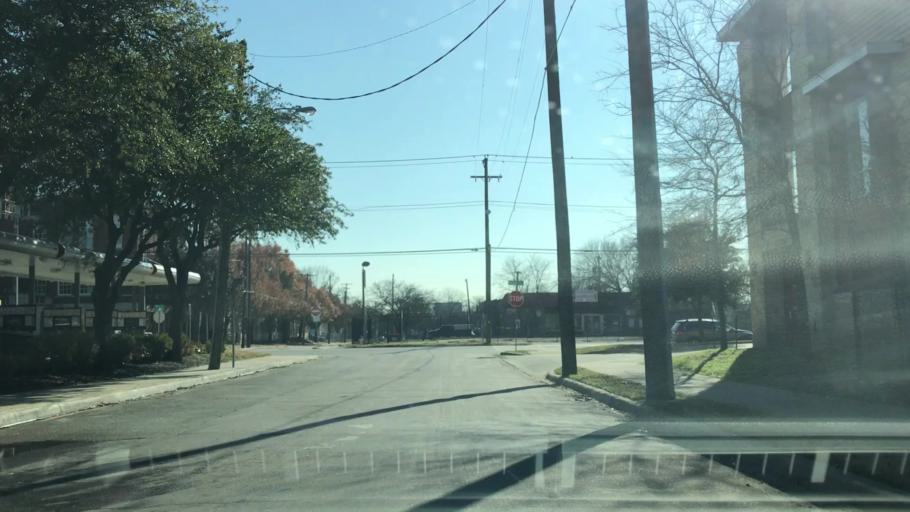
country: US
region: Texas
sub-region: Dallas County
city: Highland Park
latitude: 32.8059
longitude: -96.7774
